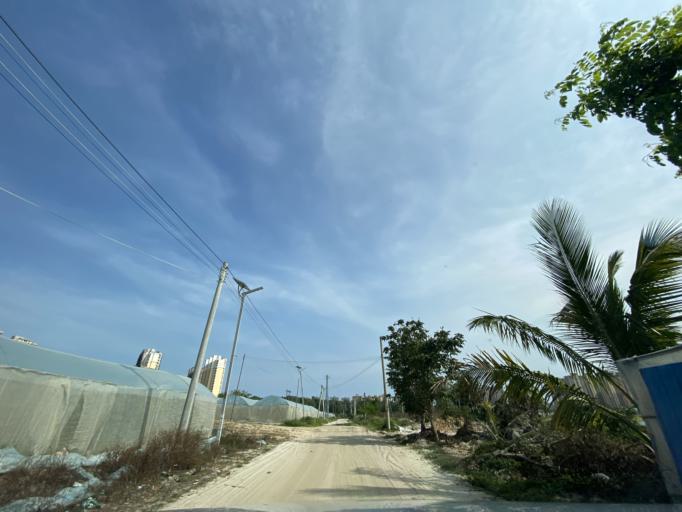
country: CN
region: Hainan
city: Yingzhou
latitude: 18.4067
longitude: 109.8363
